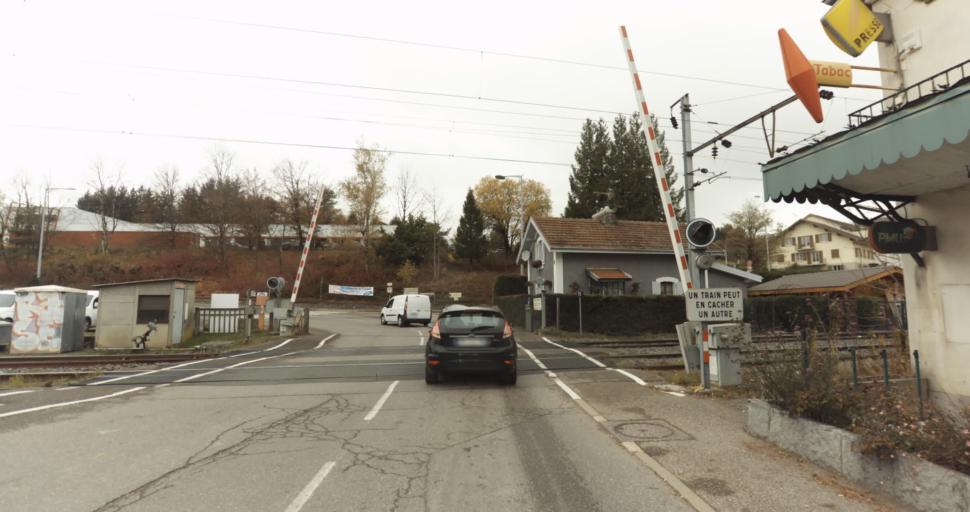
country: FR
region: Rhone-Alpes
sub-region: Departement de la Haute-Savoie
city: Groisy
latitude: 46.0118
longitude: 6.1761
